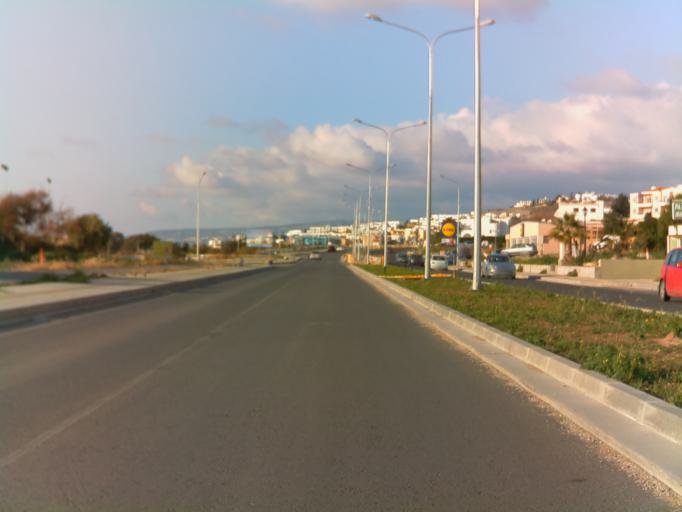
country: CY
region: Pafos
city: Paphos
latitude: 34.7791
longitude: 32.4063
